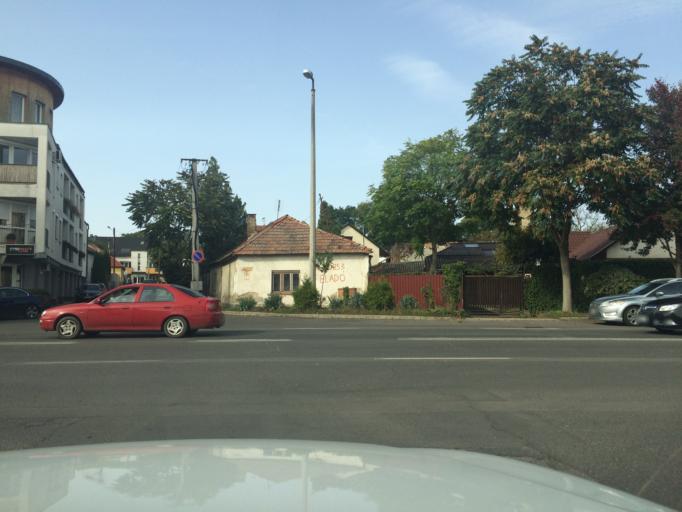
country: HU
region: Szabolcs-Szatmar-Bereg
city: Nyiregyhaza
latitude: 47.9610
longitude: 21.7226
